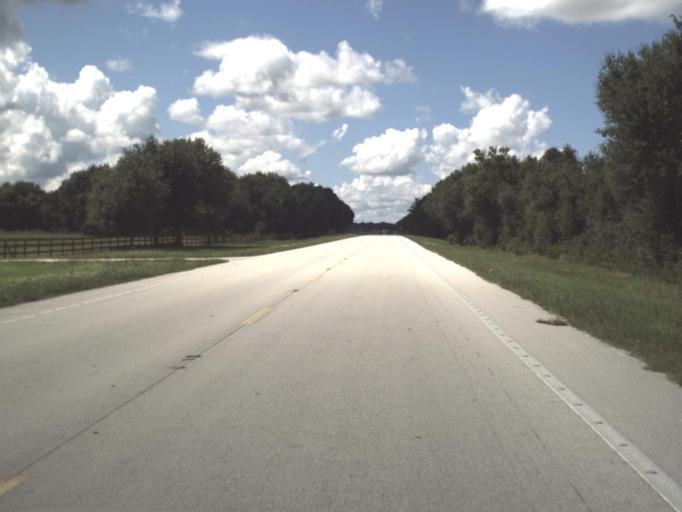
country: US
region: Florida
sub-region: DeSoto County
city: Southeast Arcadia
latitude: 27.2088
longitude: -81.7729
